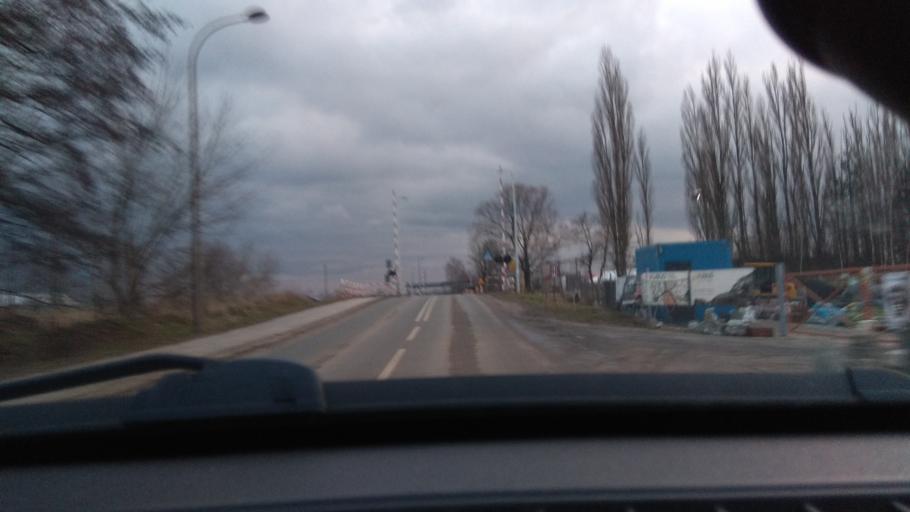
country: PL
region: Greater Poland Voivodeship
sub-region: Powiat kepinski
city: Kepno
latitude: 51.2945
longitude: 18.0061
